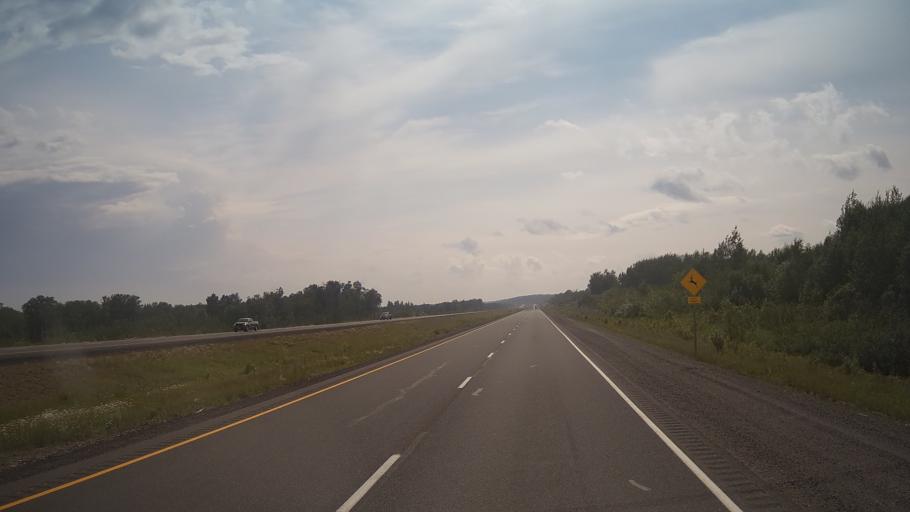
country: CA
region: Ontario
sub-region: Thunder Bay District
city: Thunder Bay
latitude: 48.5635
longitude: -88.8673
